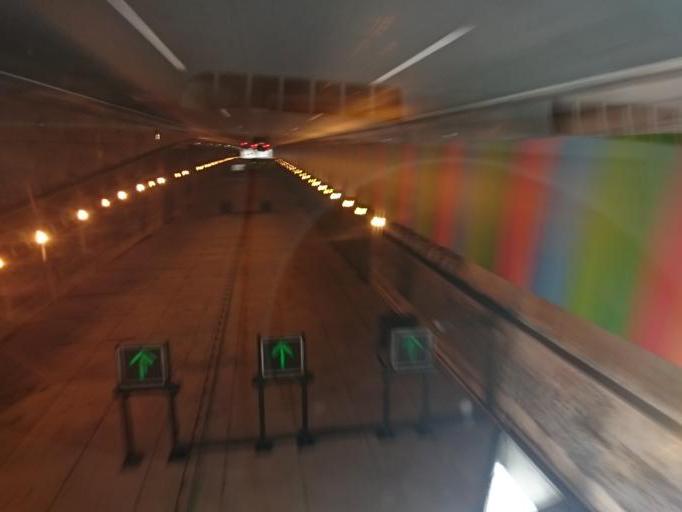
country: ES
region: Catalonia
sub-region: Provincia de Barcelona
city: L'Hospitalet de Llobregat
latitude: 41.3552
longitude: 2.1231
